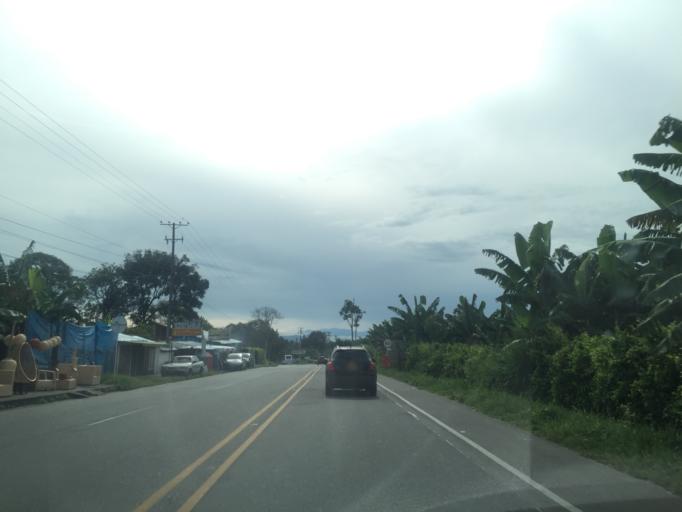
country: CO
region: Quindio
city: Armenia
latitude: 4.4945
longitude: -75.7346
